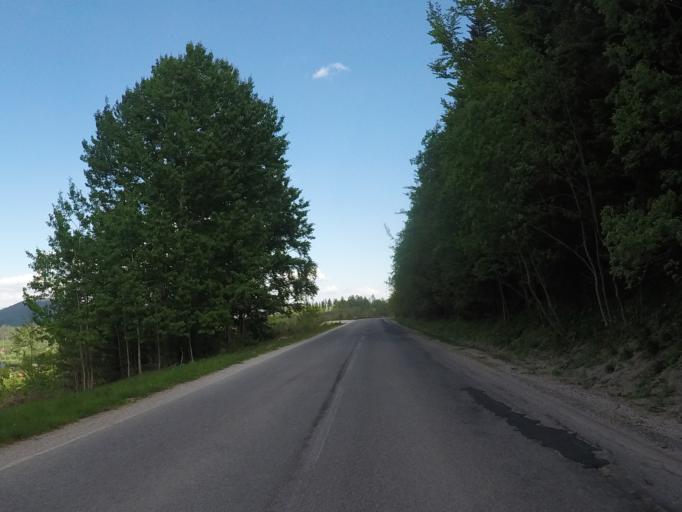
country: SK
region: Kosicky
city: Dobsina
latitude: 48.8536
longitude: 20.3614
